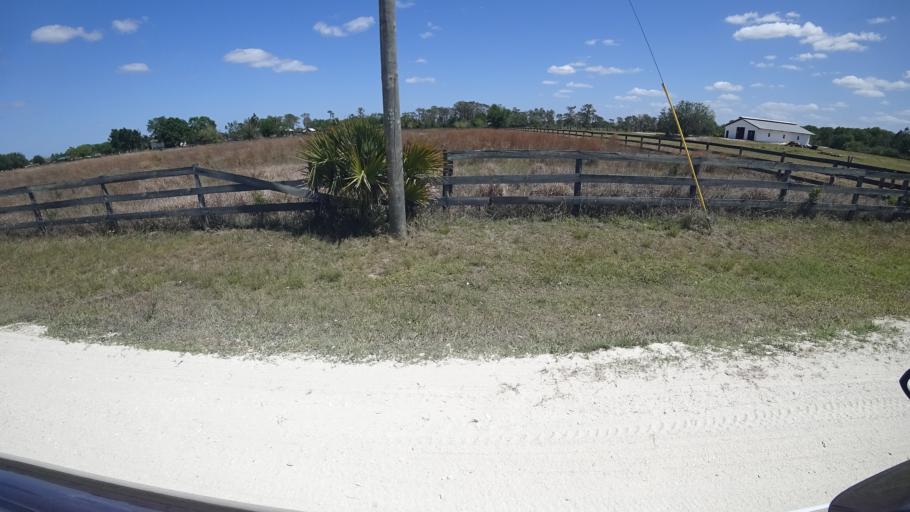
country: US
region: Florida
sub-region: Sarasota County
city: The Meadows
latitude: 27.4257
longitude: -82.3078
